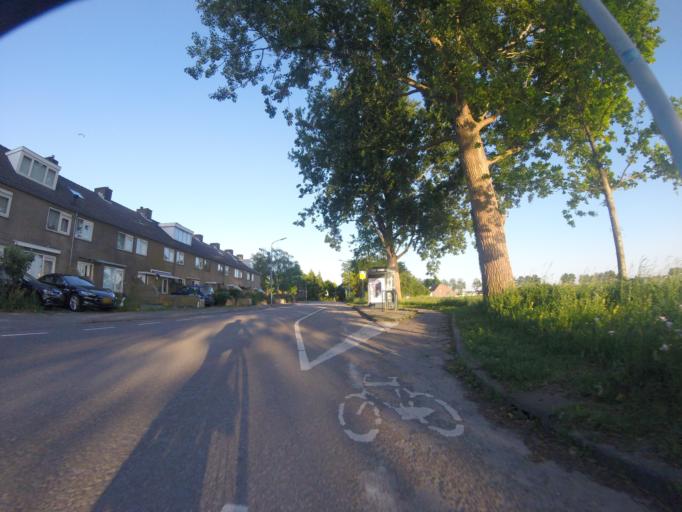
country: NL
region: North Holland
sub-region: Gemeente Haarlemmermeer
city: Hoofddorp
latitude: 52.3741
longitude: 4.7450
